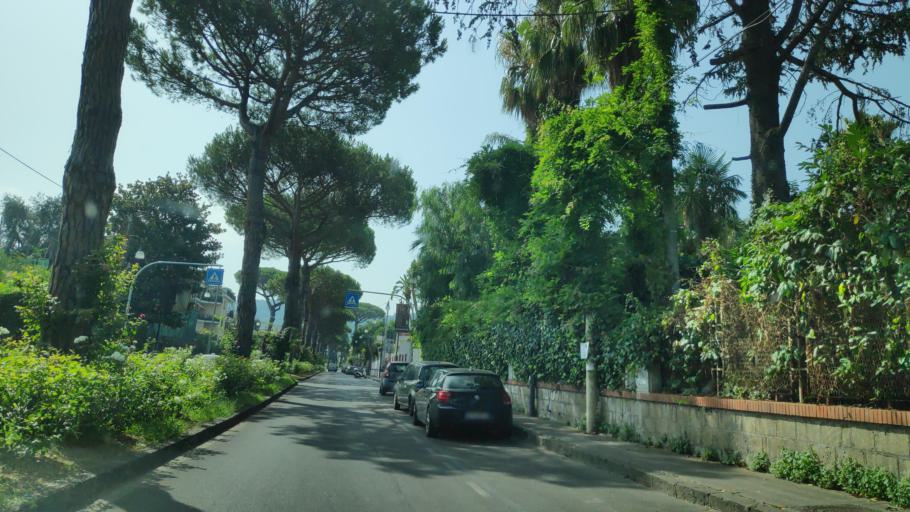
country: IT
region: Campania
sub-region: Provincia di Napoli
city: Sant'Agnello
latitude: 40.6352
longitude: 14.3950
